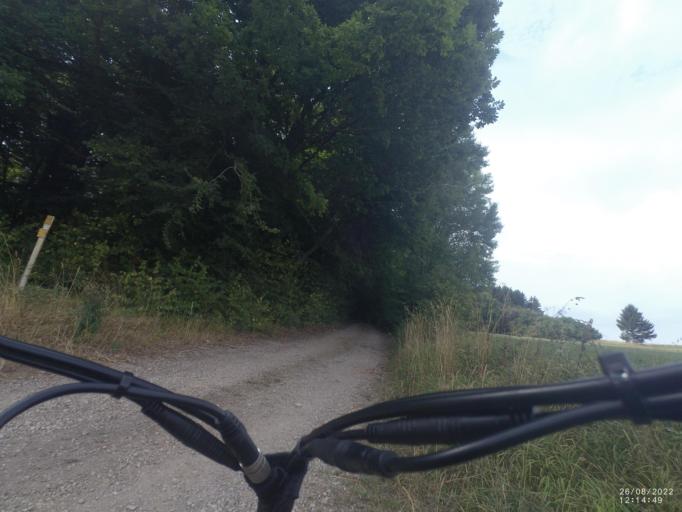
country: DE
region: Rheinland-Pfalz
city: Kalenborn-Scheuern
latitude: 50.2266
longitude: 6.5892
